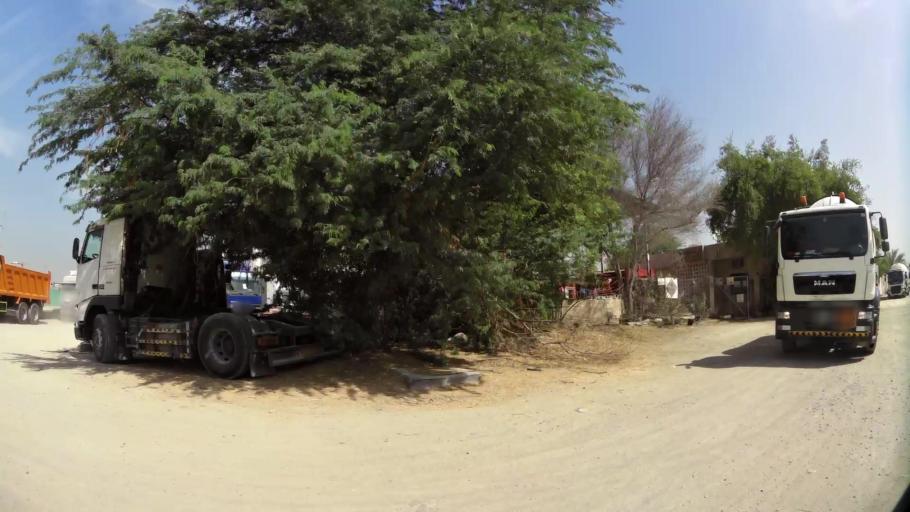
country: AE
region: Ash Shariqah
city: Sharjah
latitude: 25.2788
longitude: 55.3931
